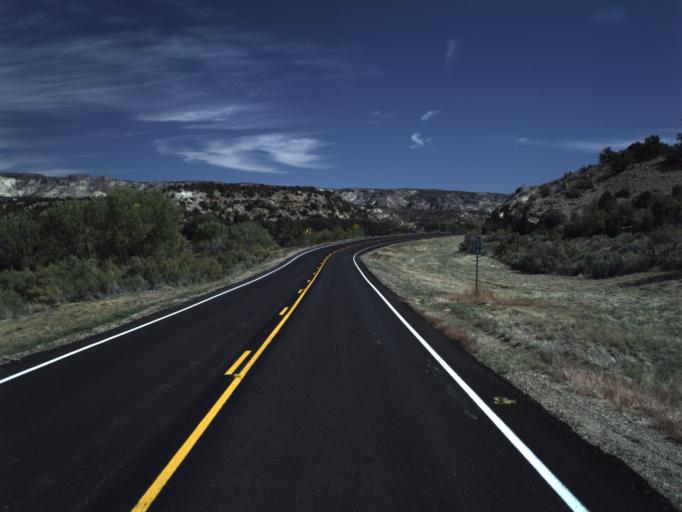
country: US
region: Utah
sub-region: Wayne County
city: Loa
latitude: 37.7714
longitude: -111.6604
